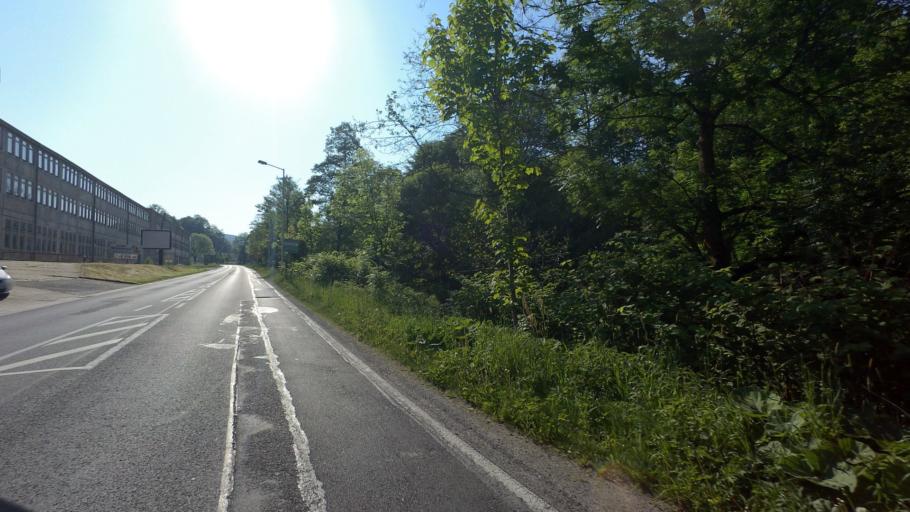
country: DE
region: Saxony
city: Sebnitz
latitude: 50.9689
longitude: 14.2517
